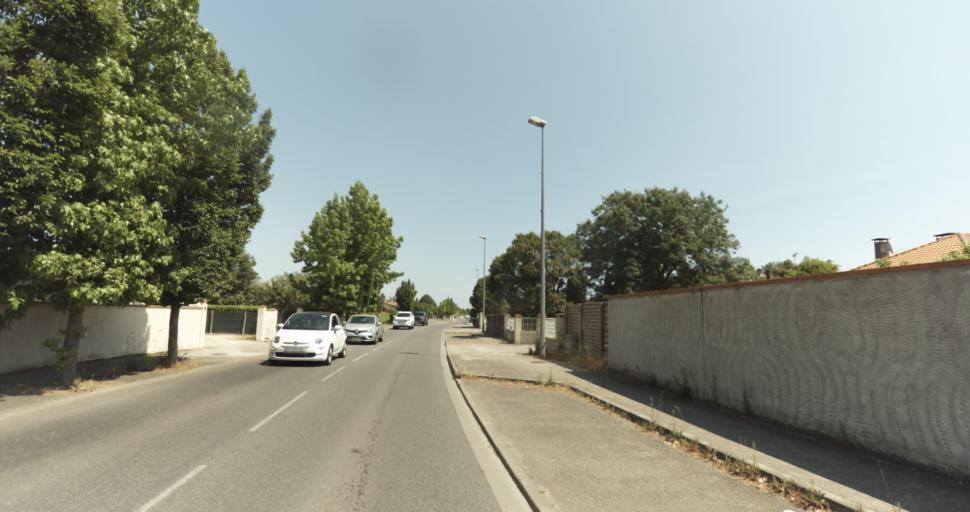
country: FR
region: Midi-Pyrenees
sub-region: Departement de la Haute-Garonne
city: La Salvetat-Saint-Gilles
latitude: 43.5683
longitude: 1.2665
